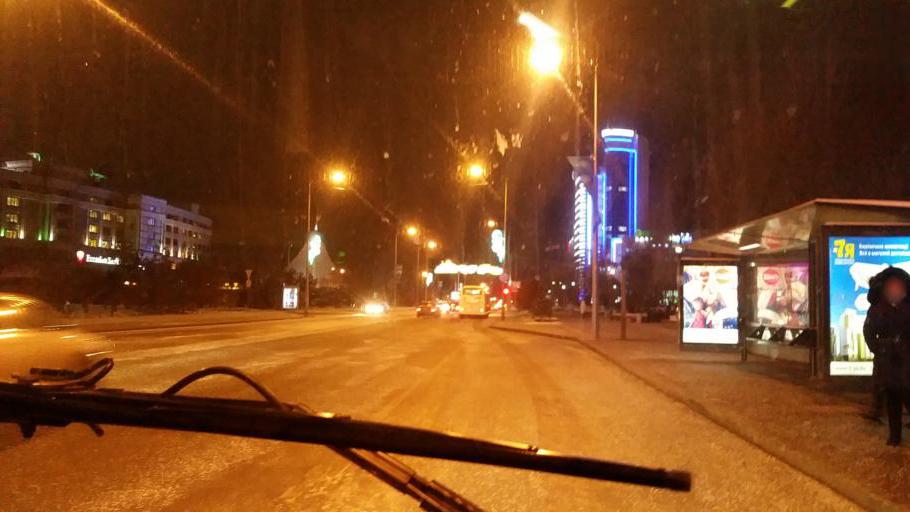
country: KZ
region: Astana Qalasy
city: Astana
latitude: 51.1328
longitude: 71.4186
